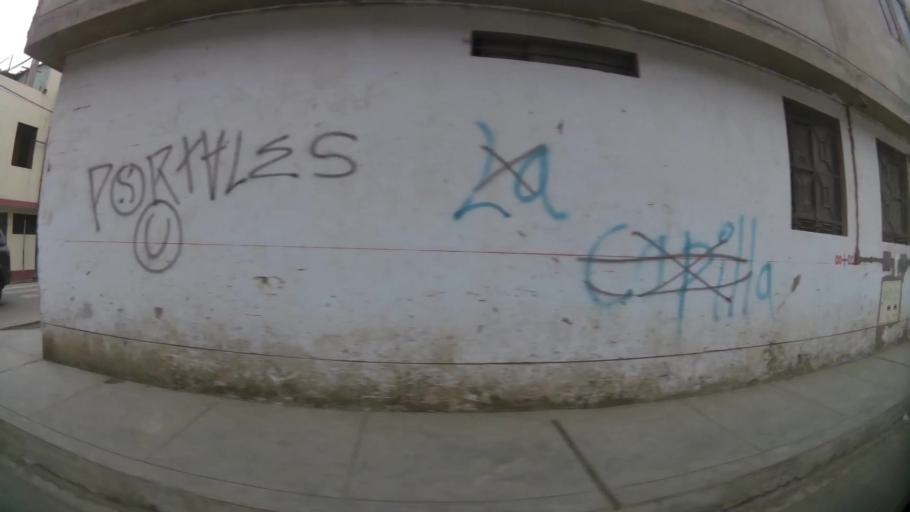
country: PE
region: Lima
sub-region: Lima
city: Independencia
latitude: -11.9751
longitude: -77.0938
